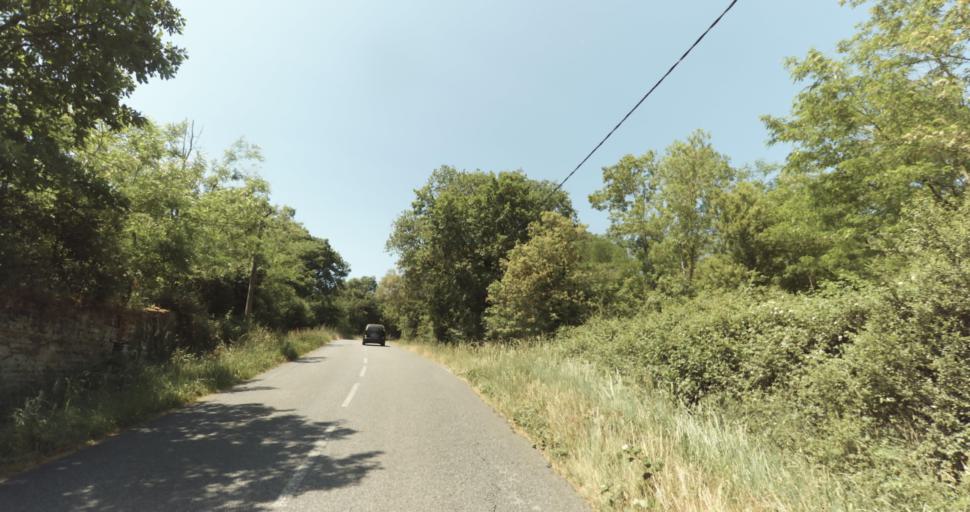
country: FR
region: Midi-Pyrenees
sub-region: Departement de la Haute-Garonne
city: La Salvetat-Saint-Gilles
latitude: 43.5982
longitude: 1.2718
